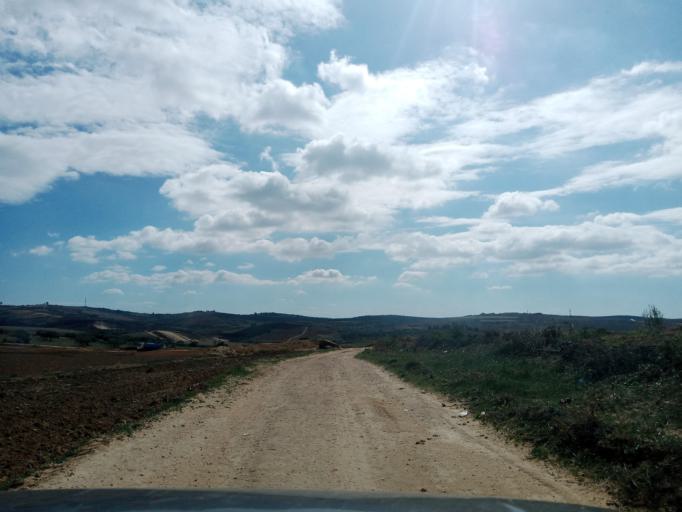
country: TN
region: Tunis
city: Oued Lill
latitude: 36.8081
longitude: 9.9850
